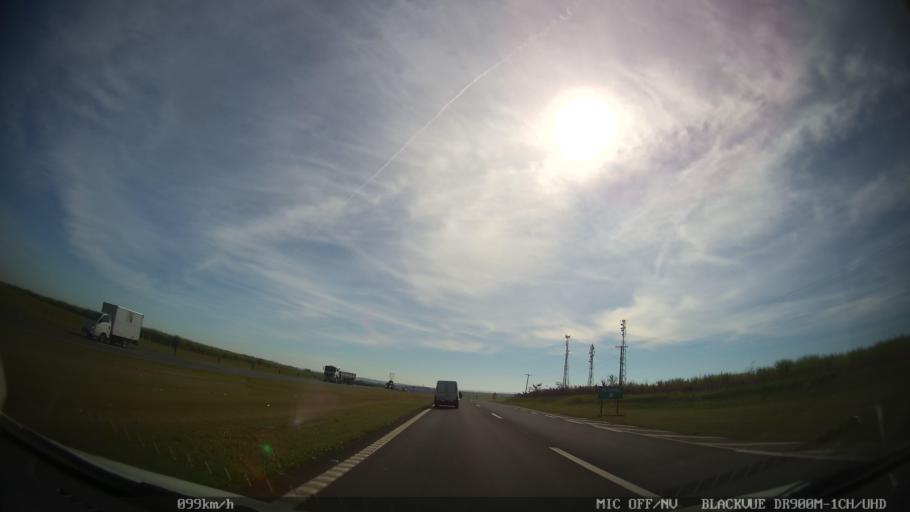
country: BR
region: Sao Paulo
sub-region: Cordeiropolis
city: Cordeiropolis
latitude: -22.4401
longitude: -47.3968
